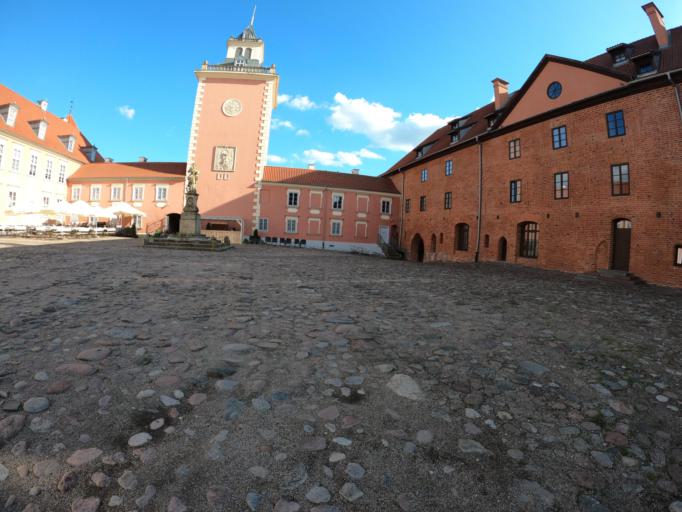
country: PL
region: Warmian-Masurian Voivodeship
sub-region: Powiat lidzbarski
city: Lidzbark Warminski
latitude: 54.1251
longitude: 20.5832
